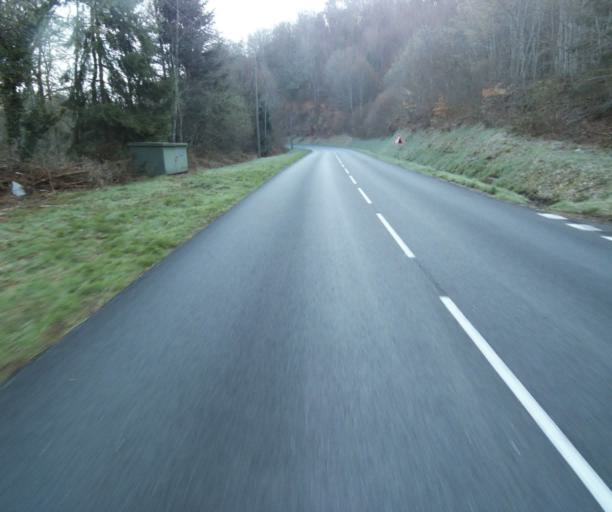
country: FR
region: Limousin
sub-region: Departement de la Correze
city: Correze
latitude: 45.3600
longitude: 1.8728
